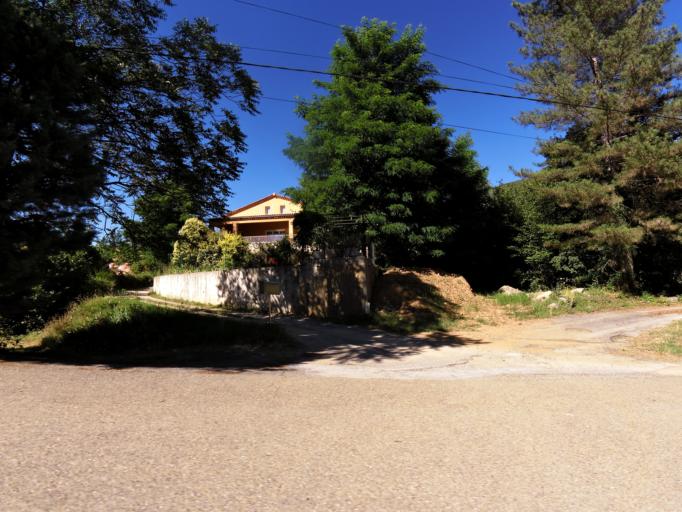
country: FR
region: Languedoc-Roussillon
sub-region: Departement du Gard
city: Saint-Jean-du-Gard
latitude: 44.1035
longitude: 3.8929
